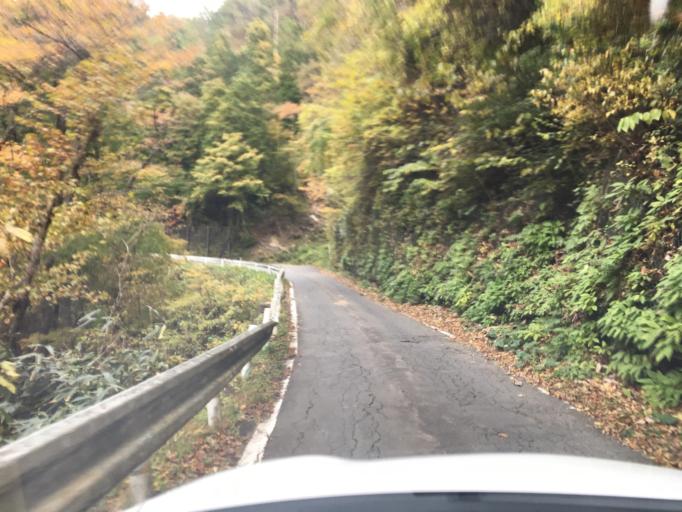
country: JP
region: Fukushima
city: Iwaki
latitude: 37.2077
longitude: 140.7601
